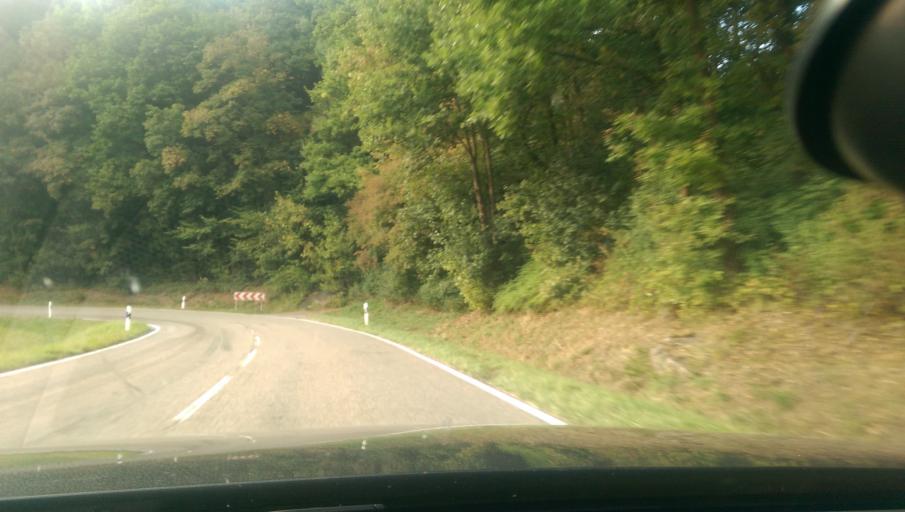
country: DE
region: Baden-Wuerttemberg
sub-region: Karlsruhe Region
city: Tiefenbronn
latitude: 48.8195
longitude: 8.8005
